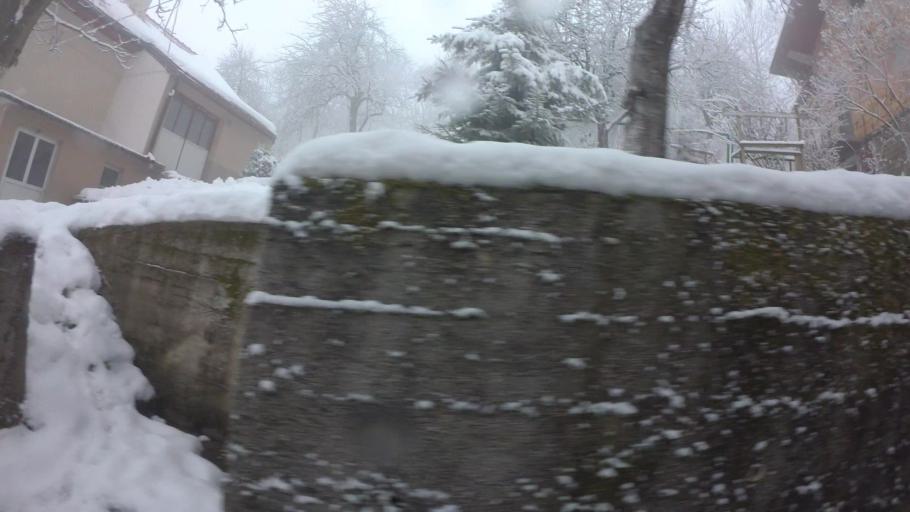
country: BA
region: Federation of Bosnia and Herzegovina
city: Kobilja Glava
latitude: 43.8490
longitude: 18.4431
